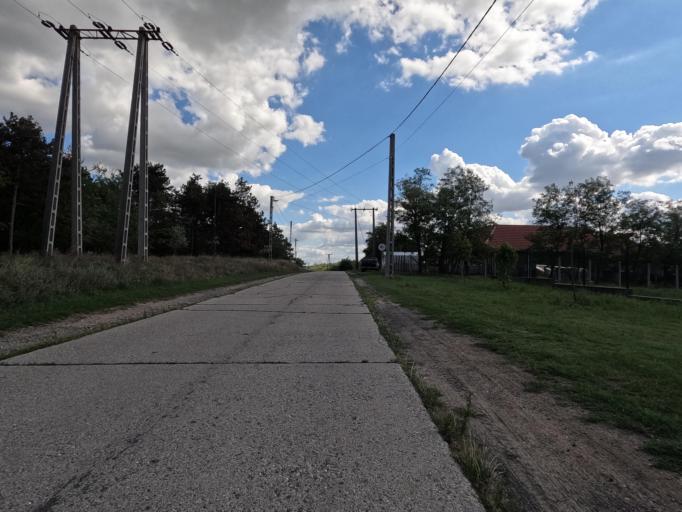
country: HU
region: Tolna
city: Paks
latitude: 46.5859
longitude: 18.8194
